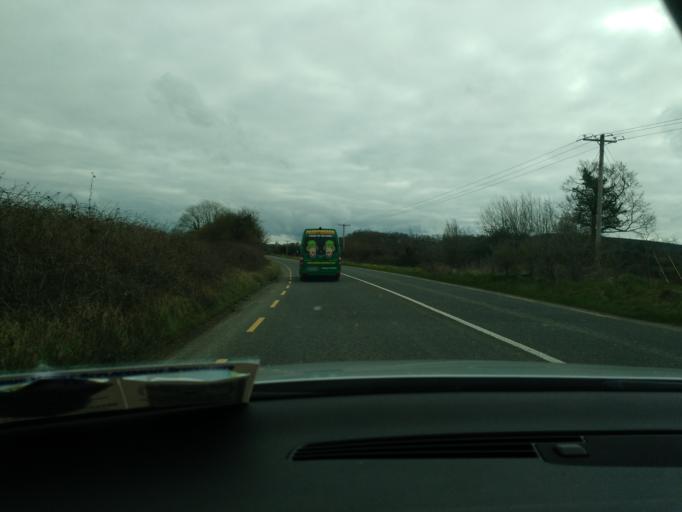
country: IE
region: Leinster
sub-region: Kilkenny
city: Ballyragget
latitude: 52.7276
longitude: -7.3766
